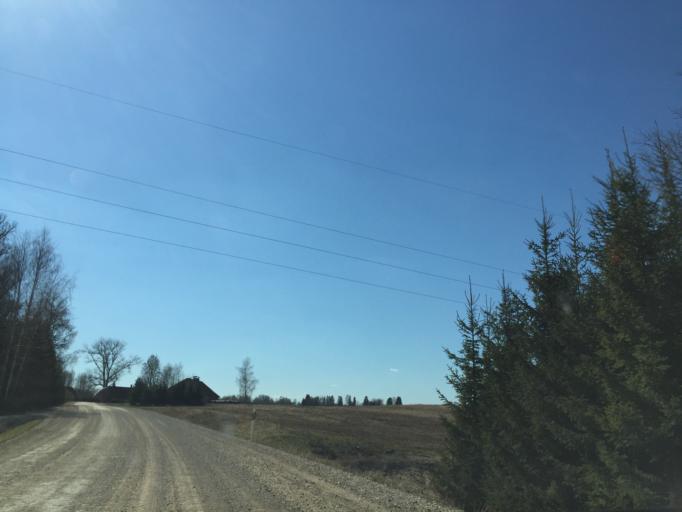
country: EE
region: Viljandimaa
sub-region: Viiratsi vald
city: Viiratsi
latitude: 58.3057
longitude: 25.6263
